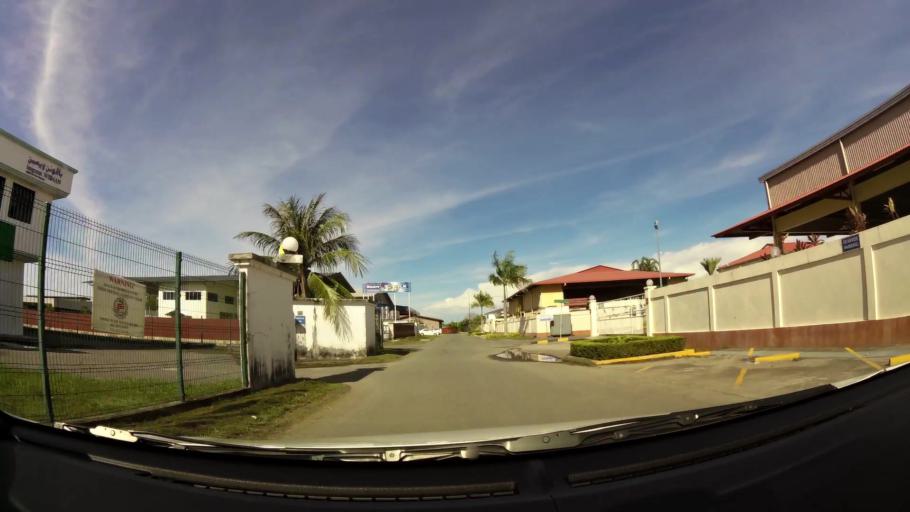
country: BN
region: Belait
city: Kuala Belait
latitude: 4.5730
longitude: 114.2073
